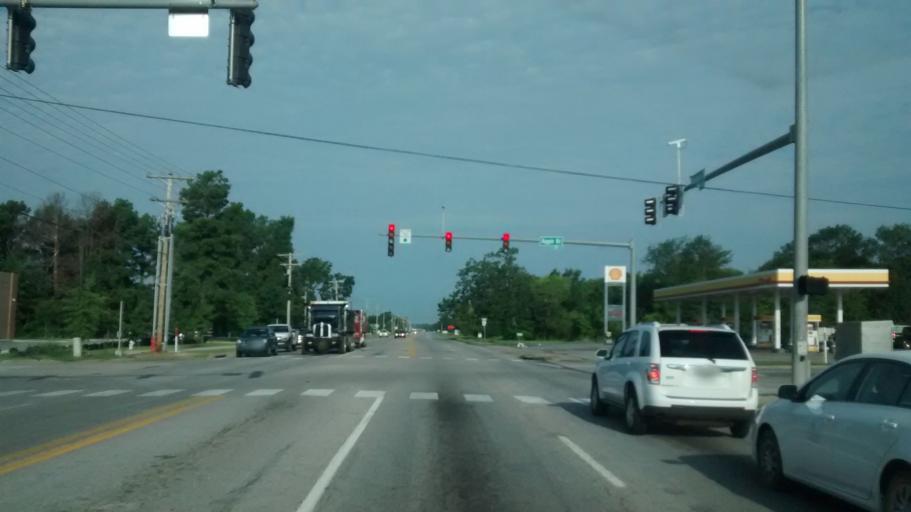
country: US
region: Arkansas
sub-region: Washington County
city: Farmington
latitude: 36.0787
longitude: -94.2171
